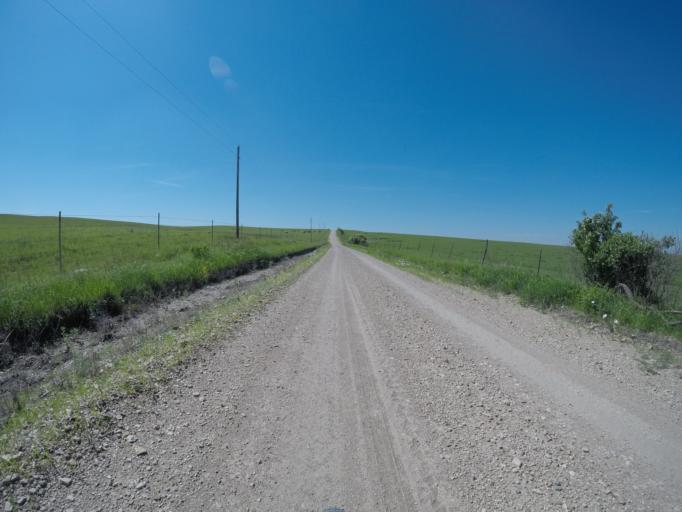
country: US
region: Kansas
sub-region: Wabaunsee County
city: Alma
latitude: 39.0051
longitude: -96.1783
